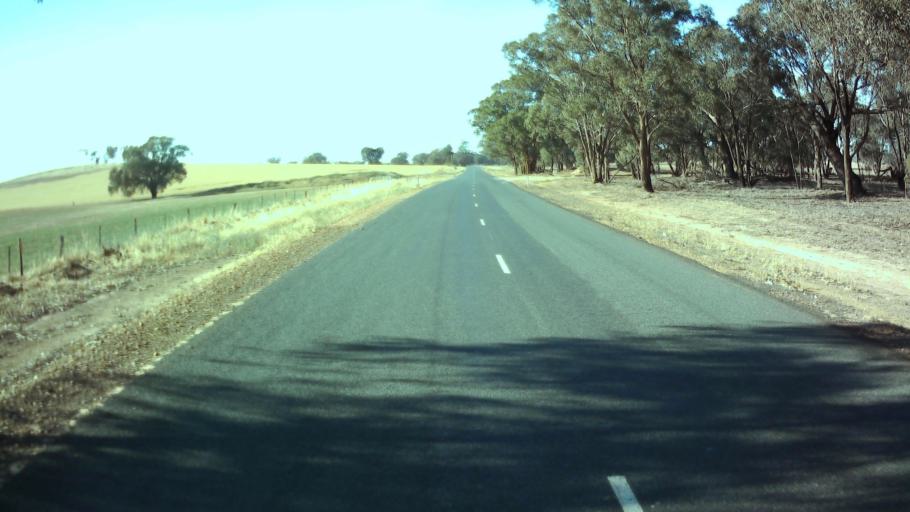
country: AU
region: New South Wales
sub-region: Weddin
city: Grenfell
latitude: -33.9676
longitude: 148.1408
